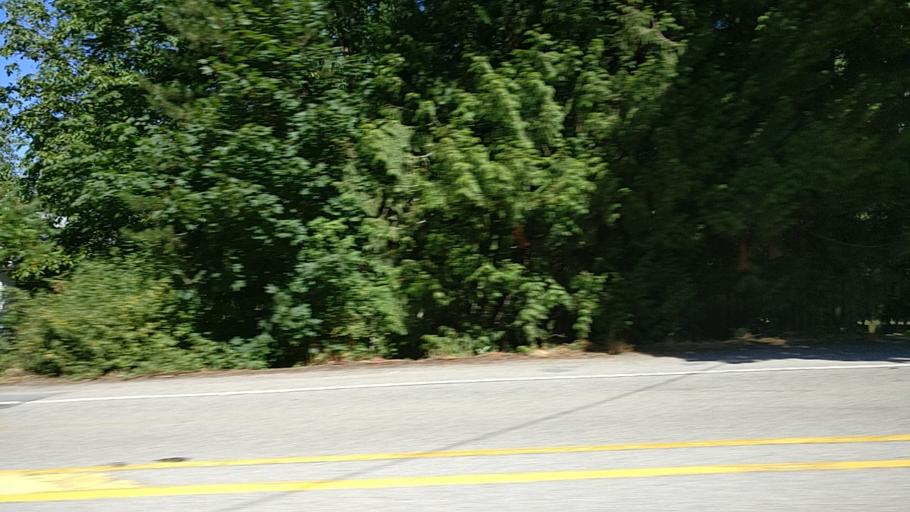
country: CA
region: British Columbia
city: Surrey
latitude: 49.0672
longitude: -122.8348
